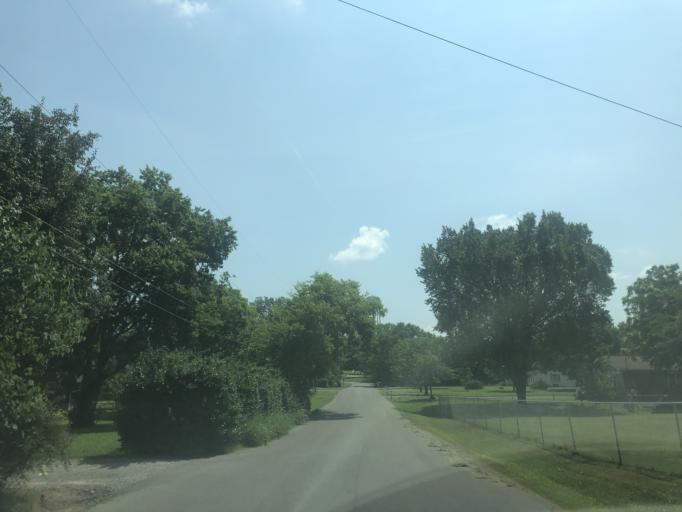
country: US
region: Tennessee
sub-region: Rutherford County
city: La Vergne
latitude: 36.0138
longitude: -86.5867
